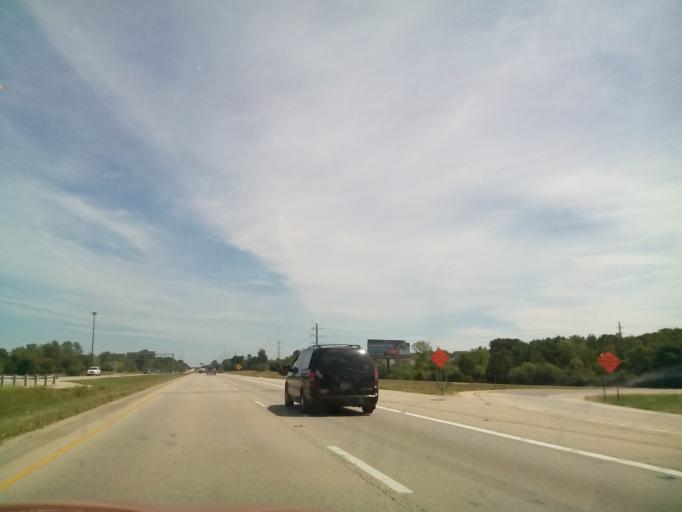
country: US
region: Illinois
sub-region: Winnebago County
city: Rockford
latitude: 42.2195
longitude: -89.0712
